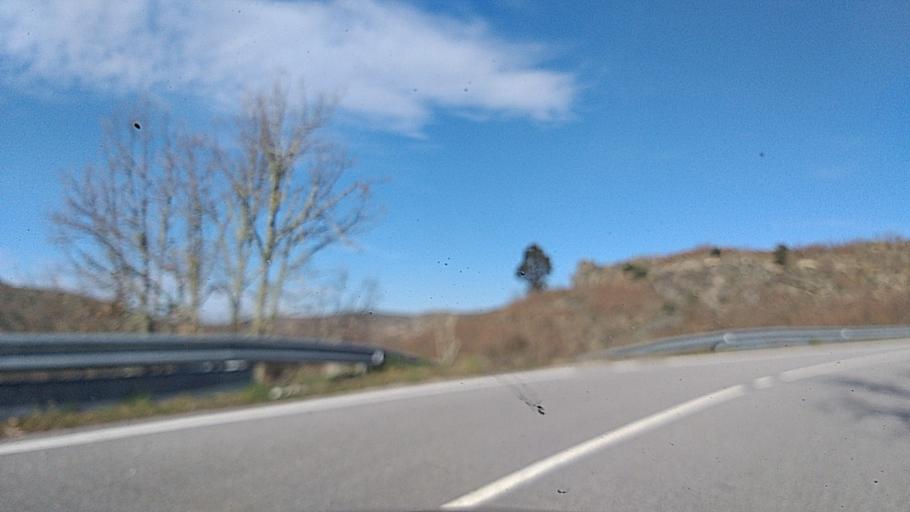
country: ES
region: Castille and Leon
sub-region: Provincia de Salamanca
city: Fuentes de Onoro
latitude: 40.6171
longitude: -6.9162
